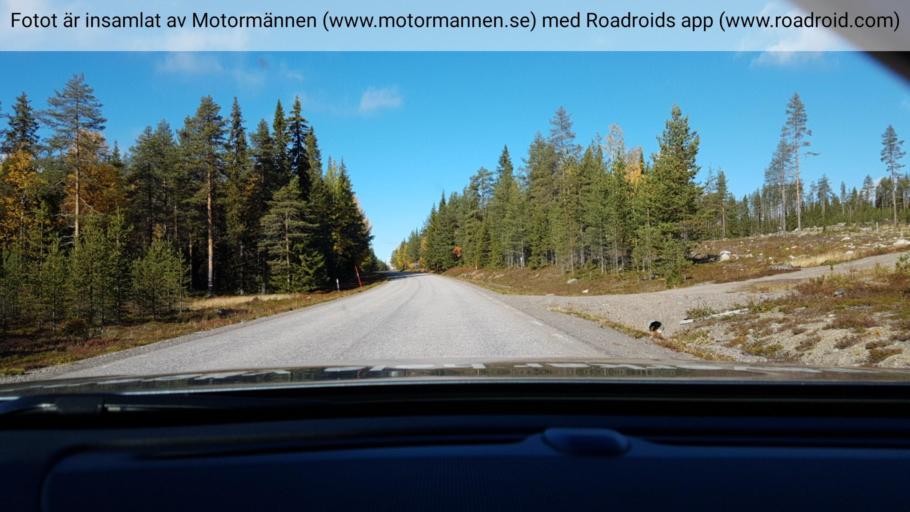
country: SE
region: Vaesterbotten
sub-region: Mala Kommun
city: Mala
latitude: 65.7658
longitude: 18.5486
